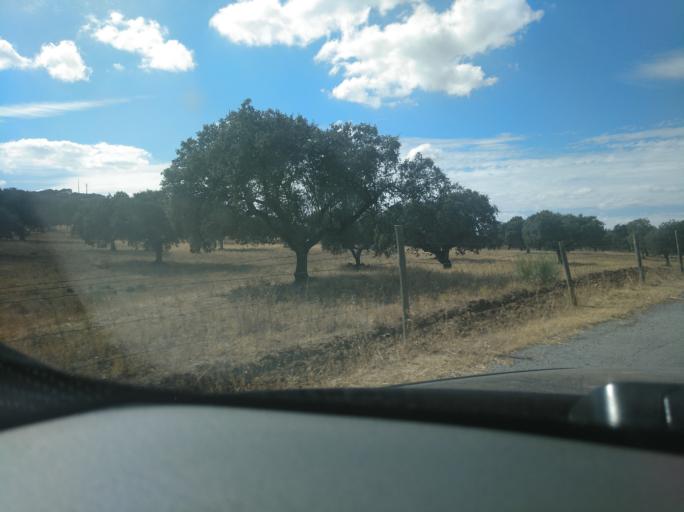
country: ES
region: Extremadura
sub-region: Provincia de Badajoz
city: La Codosera
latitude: 39.1163
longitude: -7.1516
